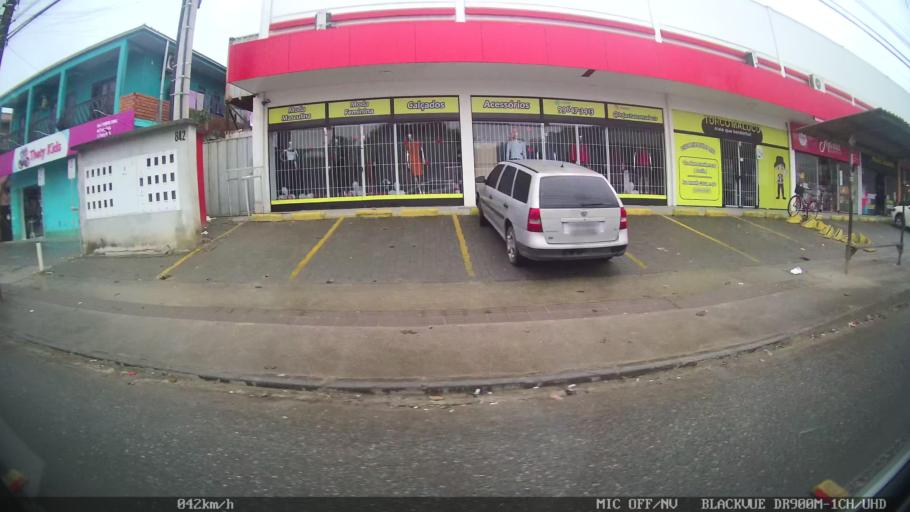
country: BR
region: Santa Catarina
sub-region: Joinville
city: Joinville
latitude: -26.2119
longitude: -48.8243
